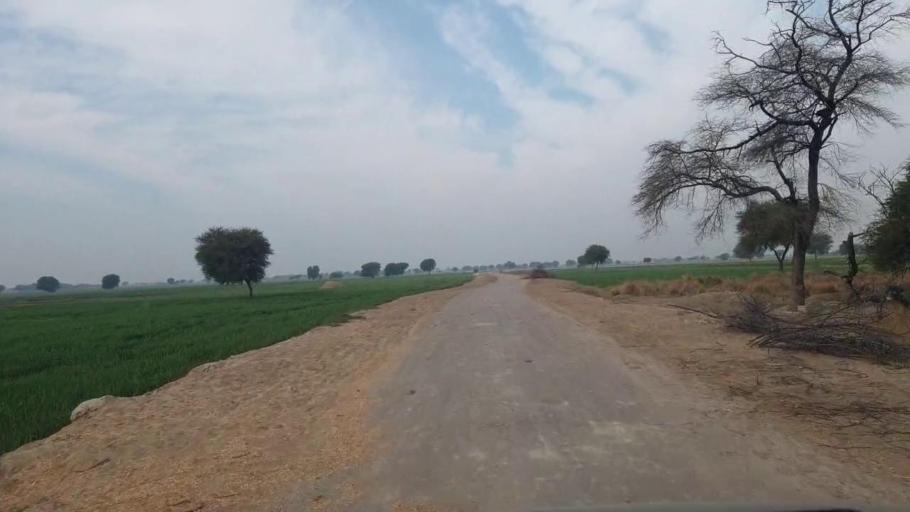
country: PK
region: Sindh
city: Shahdadpur
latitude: 25.9502
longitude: 68.6752
